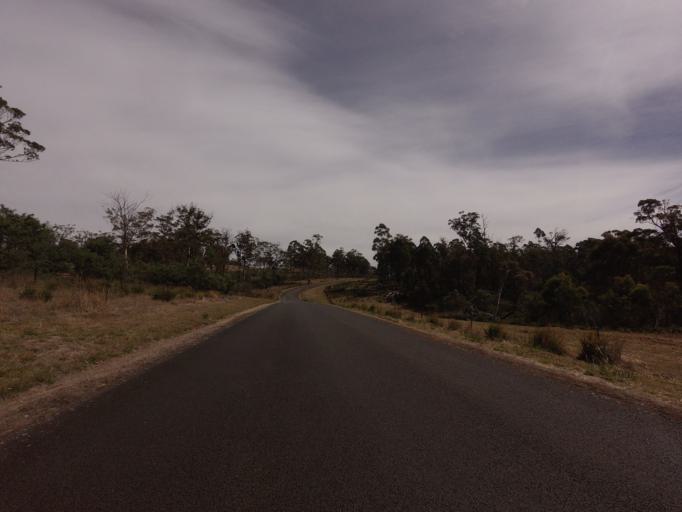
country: AU
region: Tasmania
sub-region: Sorell
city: Sorell
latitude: -42.5525
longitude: 147.6738
